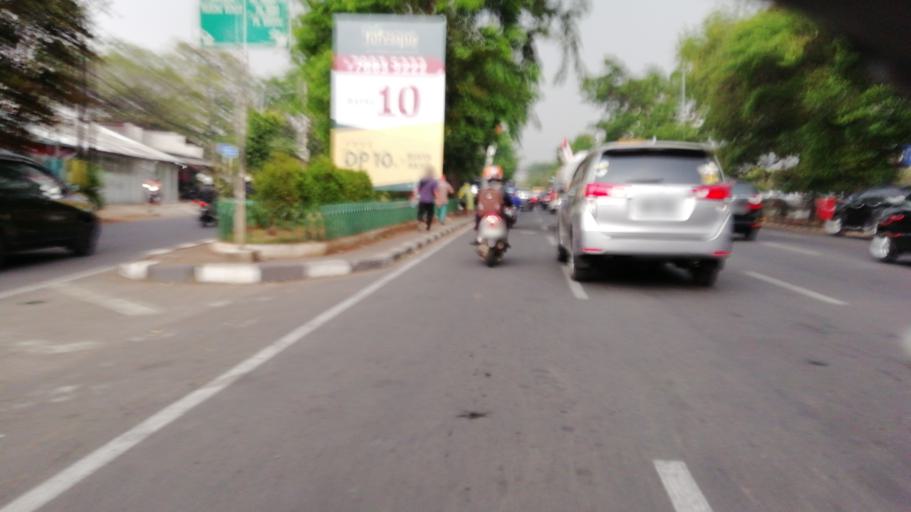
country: ID
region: Jakarta Raya
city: Jakarta
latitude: -6.2932
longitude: 106.8218
